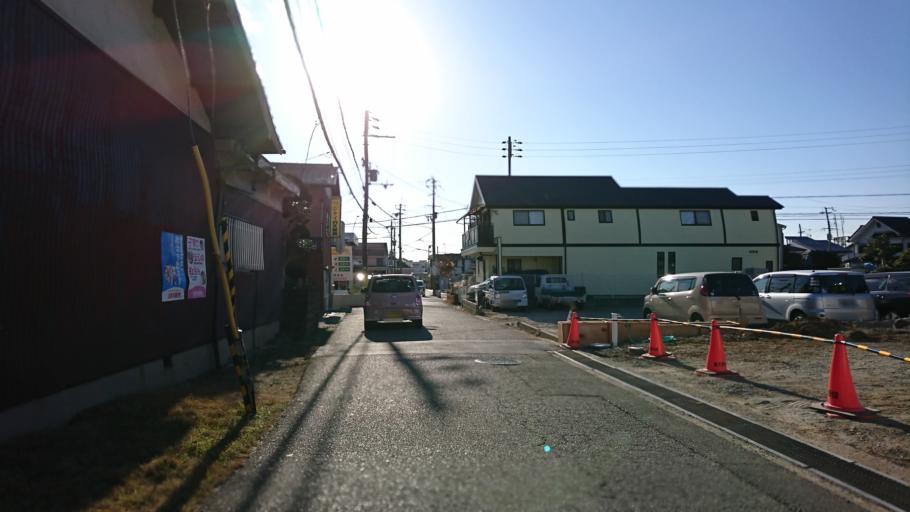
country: JP
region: Hyogo
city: Kakogawacho-honmachi
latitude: 34.7426
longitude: 134.8453
